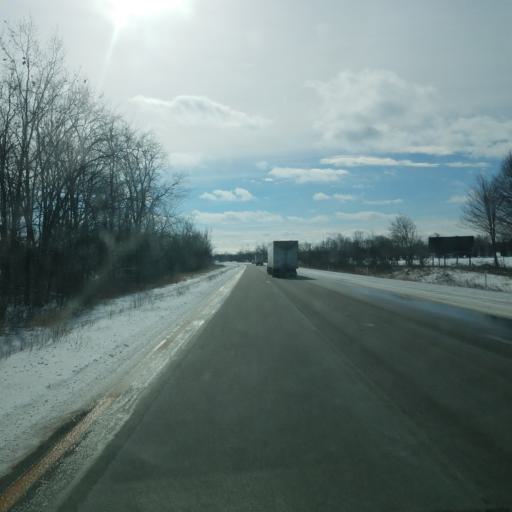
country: US
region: Michigan
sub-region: Gratiot County
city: Ithaca
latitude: 43.3172
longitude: -84.6022
